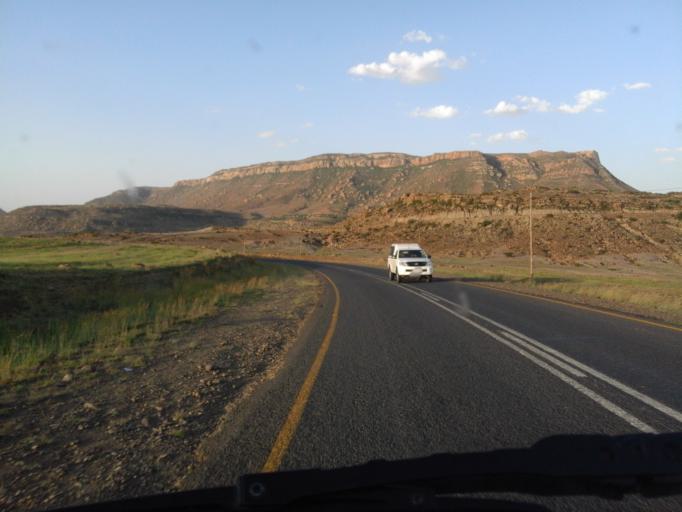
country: LS
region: Mafeteng
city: Mafeteng
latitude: -29.8956
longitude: 27.2556
